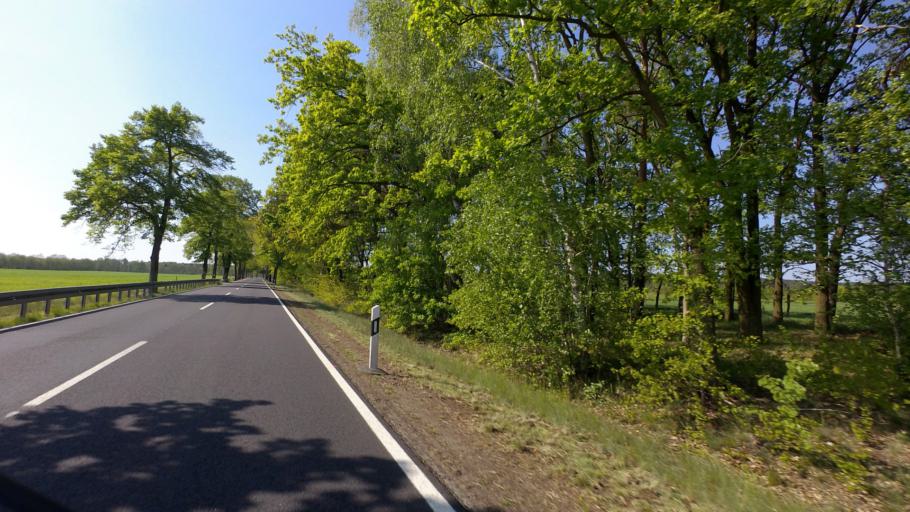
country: DE
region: Brandenburg
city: Munchehofe
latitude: 52.0914
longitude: 13.8542
